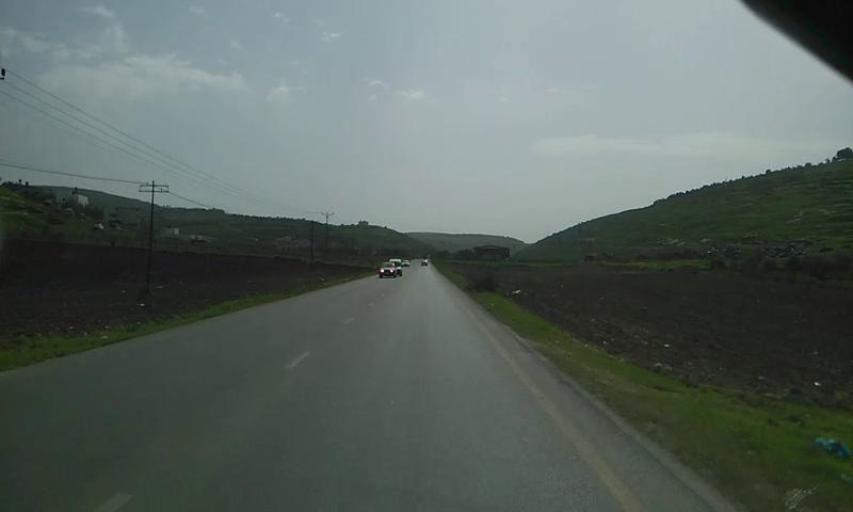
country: PS
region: West Bank
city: Mirkah
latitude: 32.3960
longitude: 35.2217
